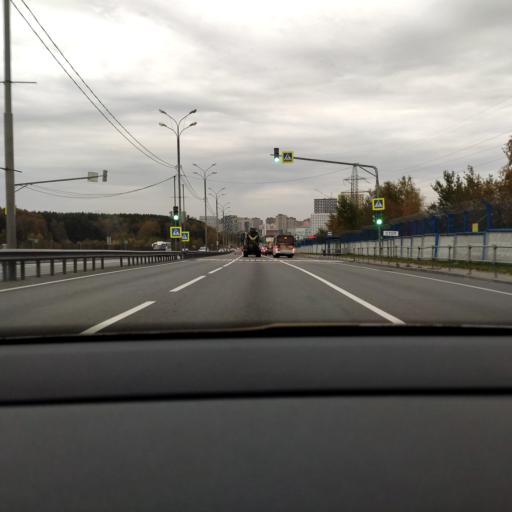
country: RU
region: Moskovskaya
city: Mytishchi
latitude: 55.9217
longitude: 37.6982
